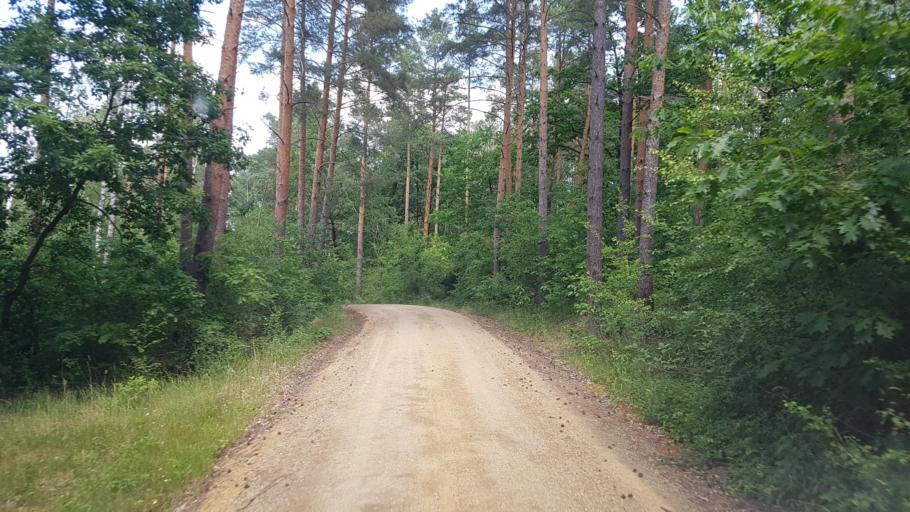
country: DE
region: Brandenburg
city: Plessa
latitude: 51.4927
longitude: 13.6216
